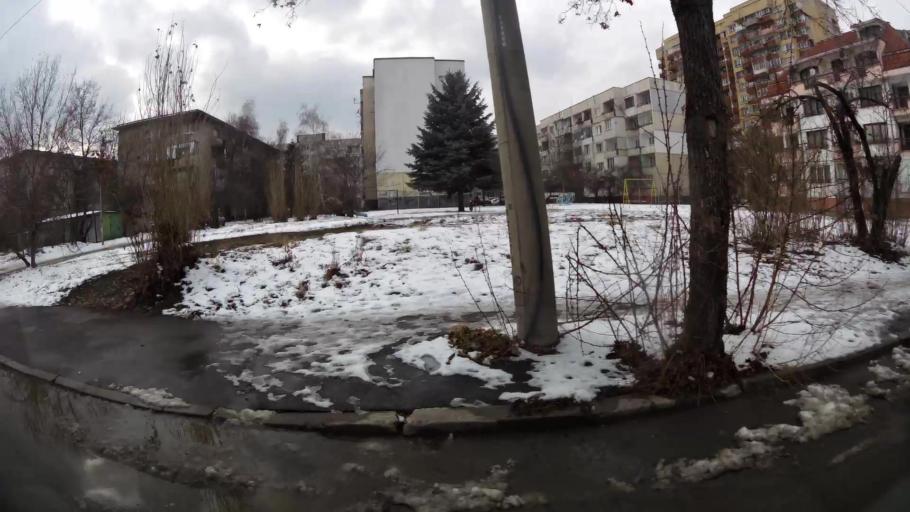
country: BG
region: Sofia-Capital
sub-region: Stolichna Obshtina
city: Sofia
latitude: 42.7015
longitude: 23.3661
